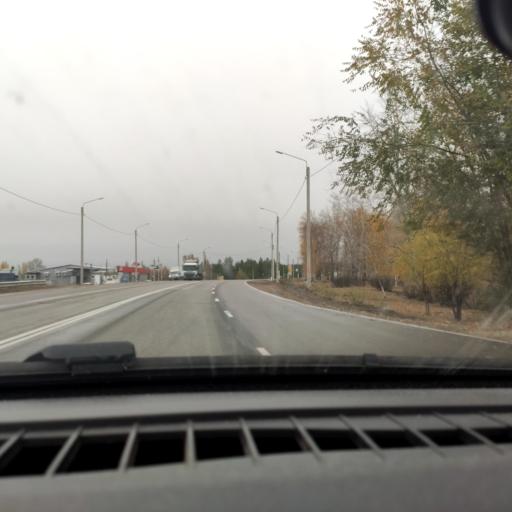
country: RU
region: Voronezj
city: Uryv-Pokrovka
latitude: 51.0439
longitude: 38.9817
